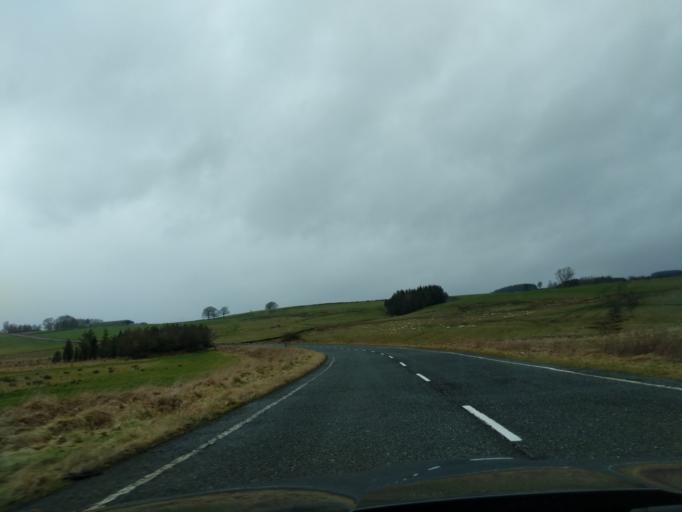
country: GB
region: England
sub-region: Northumberland
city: Otterburn
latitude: 55.2233
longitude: -2.1414
